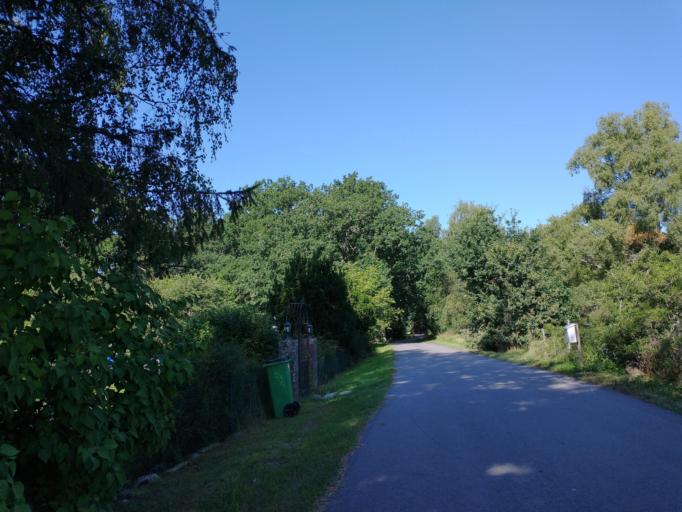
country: SE
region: Kalmar
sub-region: Kalmar Kommun
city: Lindsdal
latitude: 56.7837
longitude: 16.2768
